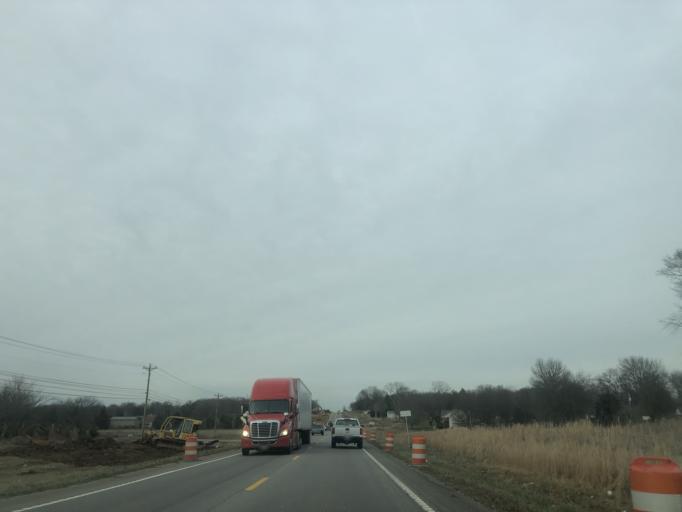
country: US
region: Tennessee
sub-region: Wilson County
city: Mount Juliet
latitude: 36.2665
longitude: -86.4407
